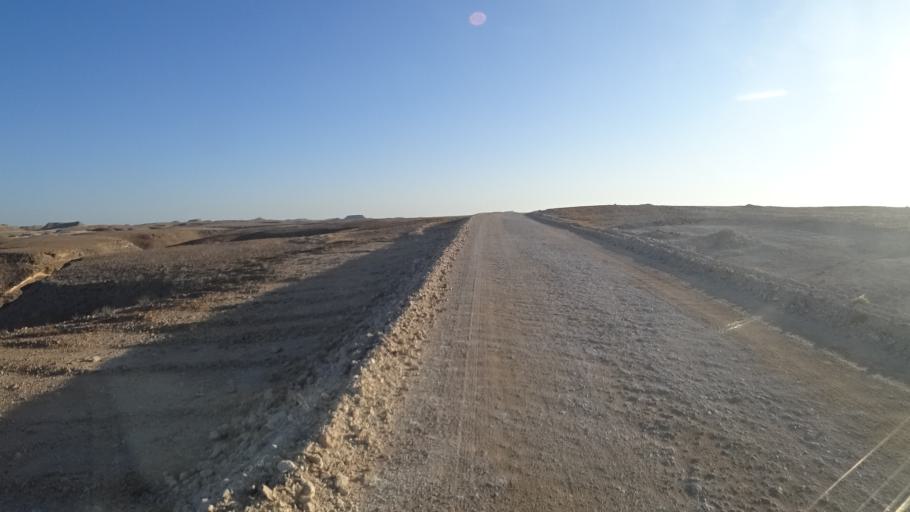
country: YE
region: Al Mahrah
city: Hawf
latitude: 17.1592
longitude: 53.3504
